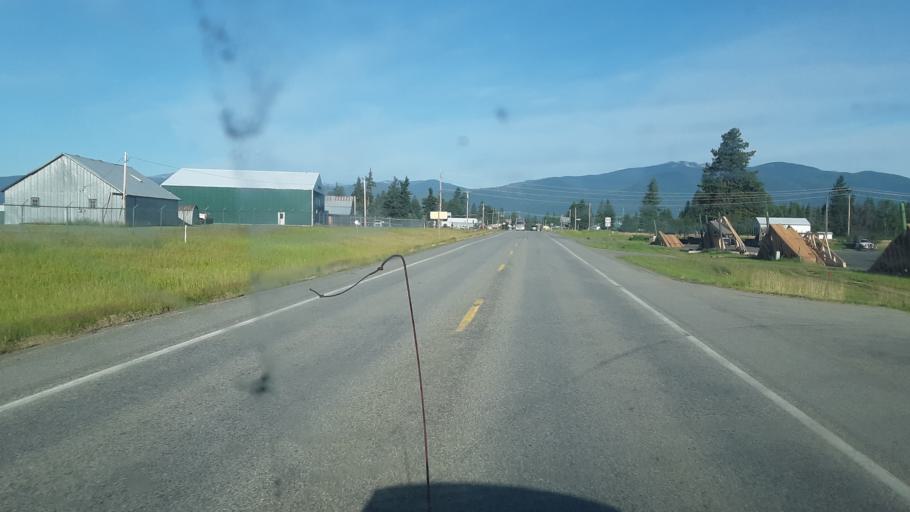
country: US
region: Idaho
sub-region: Boundary County
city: Bonners Ferry
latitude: 48.7313
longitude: -116.2902
